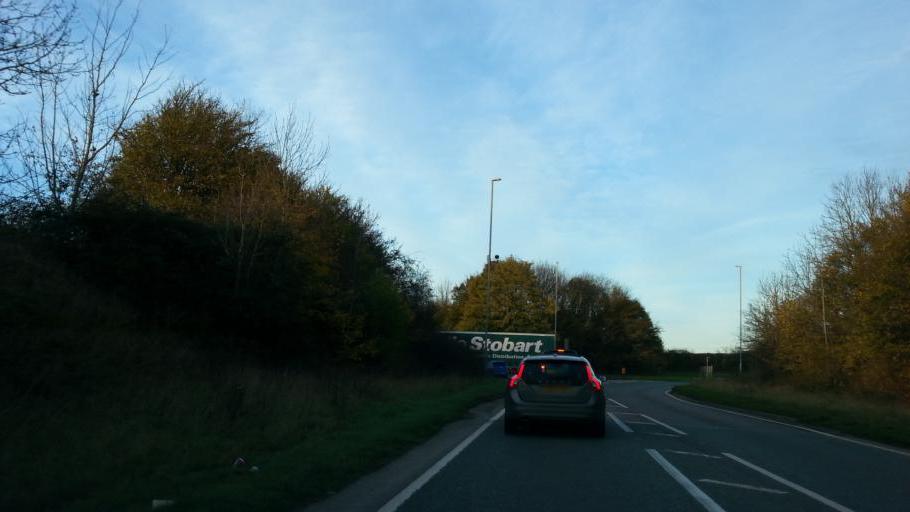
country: GB
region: England
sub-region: District of Rutland
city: Ketton
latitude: 52.5987
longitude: -0.5359
